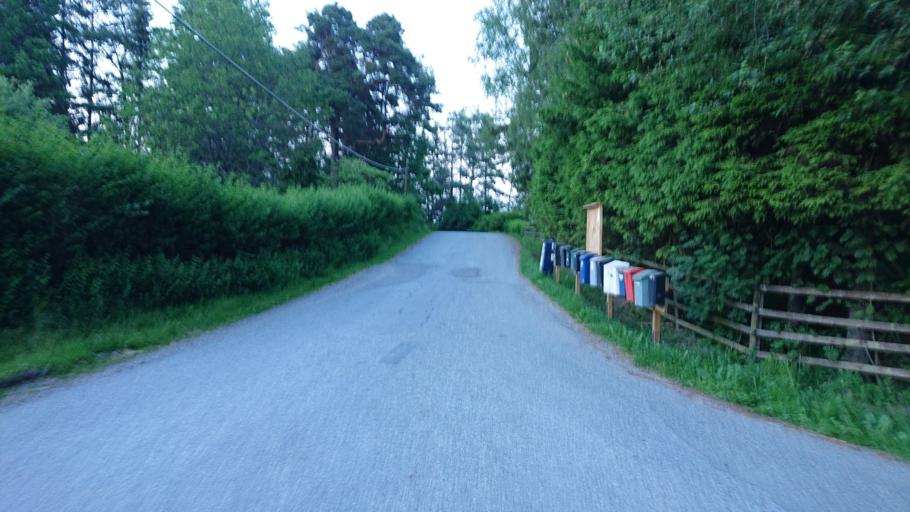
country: SE
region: Stockholm
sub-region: Osterakers Kommun
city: Akersberga
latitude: 59.4731
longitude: 18.2398
